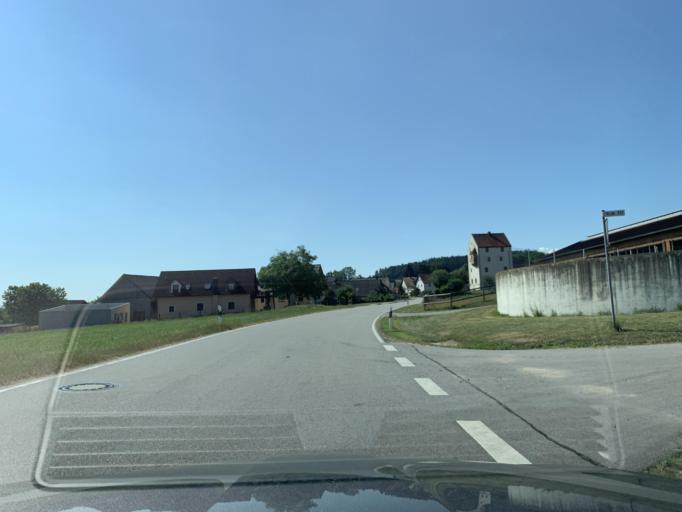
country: DE
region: Bavaria
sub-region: Upper Palatinate
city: Pettendorf
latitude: 49.3561
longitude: 12.3594
